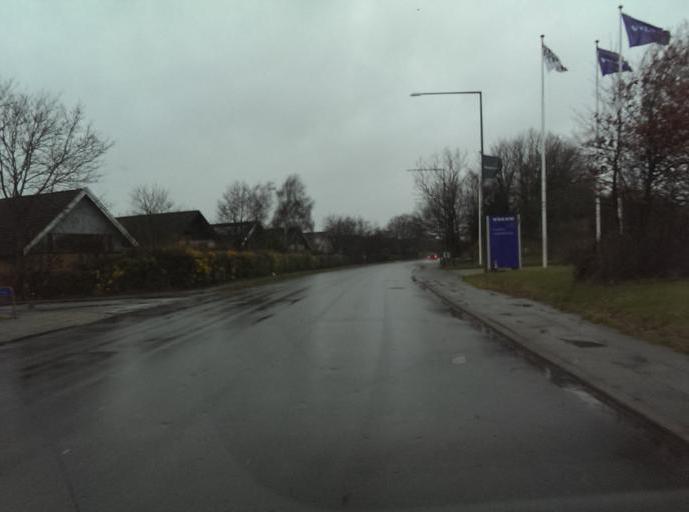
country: DK
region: South Denmark
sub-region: Esbjerg Kommune
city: Esbjerg
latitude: 55.4811
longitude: 8.4964
